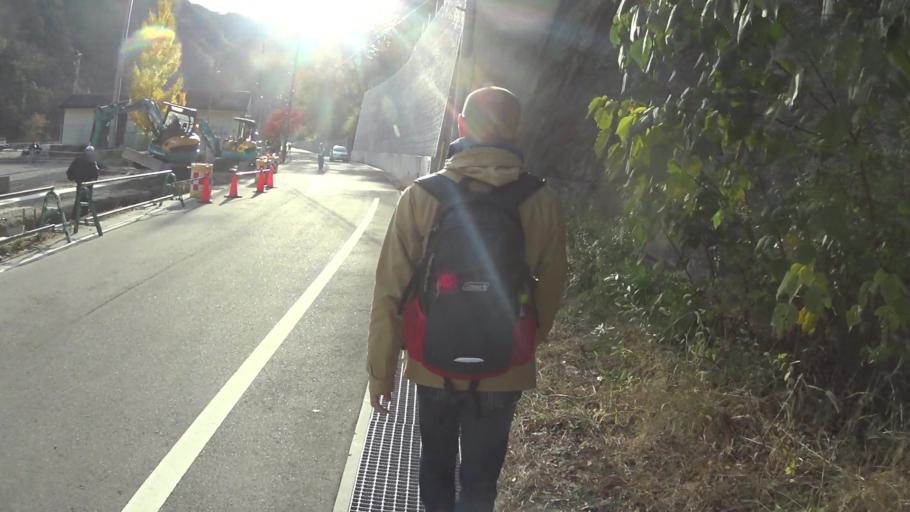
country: JP
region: Hyogo
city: Takarazuka
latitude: 34.8582
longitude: 135.3108
